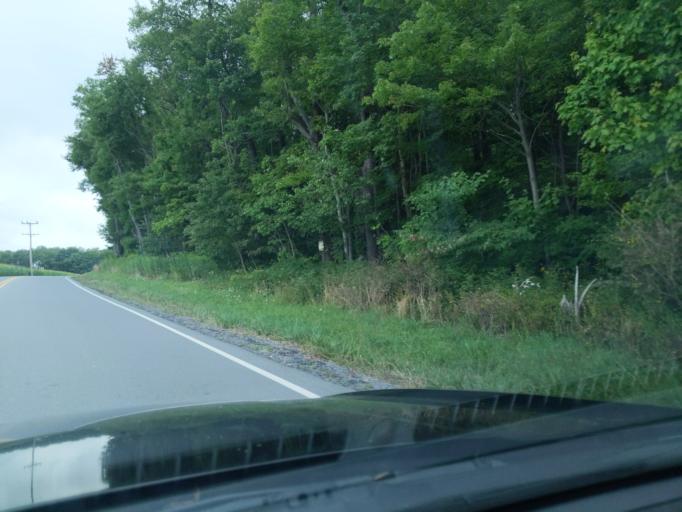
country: US
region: Pennsylvania
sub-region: Cambria County
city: Beaverdale
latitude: 40.3140
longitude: -78.5739
